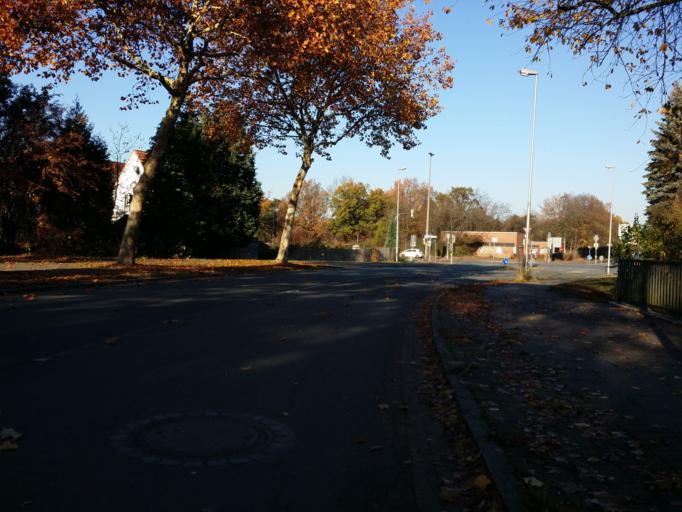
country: DE
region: Lower Saxony
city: Lilienthal
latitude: 53.0707
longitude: 8.9023
